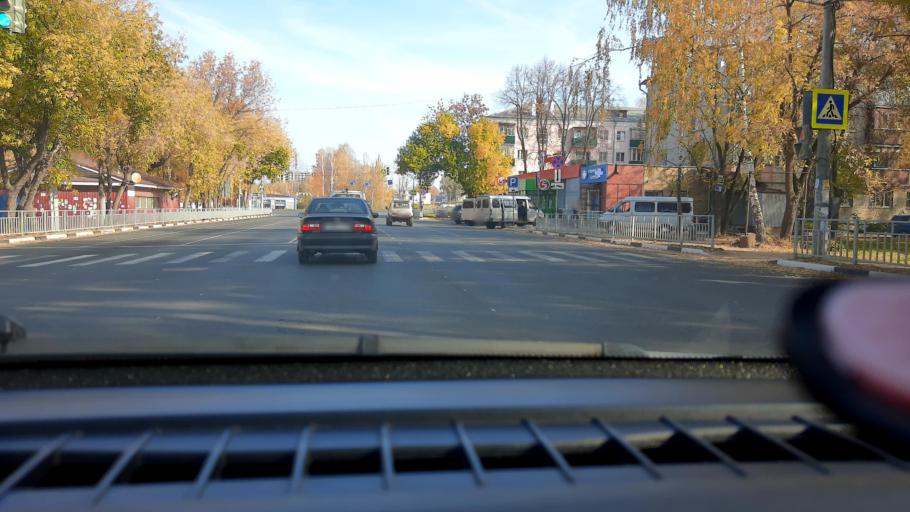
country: RU
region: Nizjnij Novgorod
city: Kstovo
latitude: 56.1560
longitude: 44.1963
